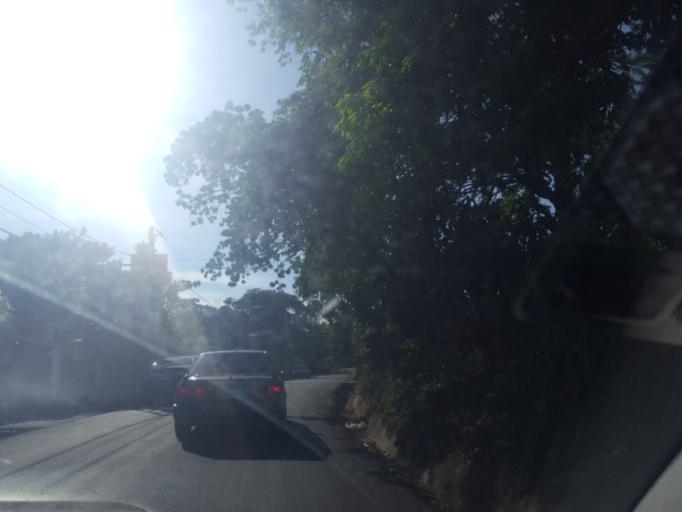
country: DO
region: La Vega
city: Rio Verde Arriba
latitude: 19.3474
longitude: -70.6247
